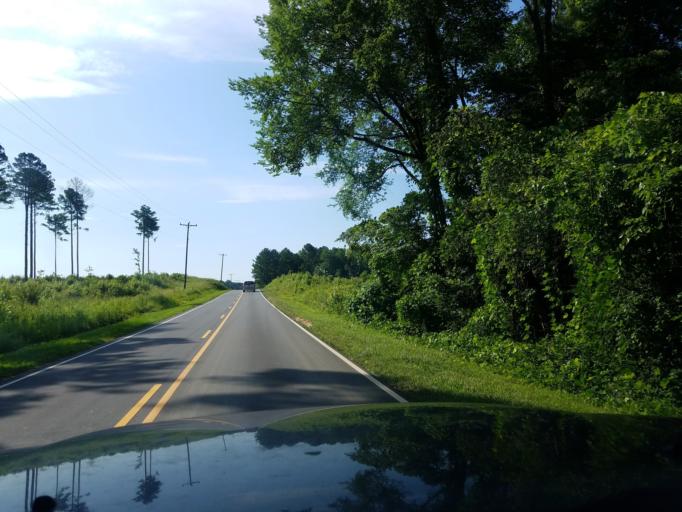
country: US
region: North Carolina
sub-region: Granville County
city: Butner
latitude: 36.1711
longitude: -78.7911
